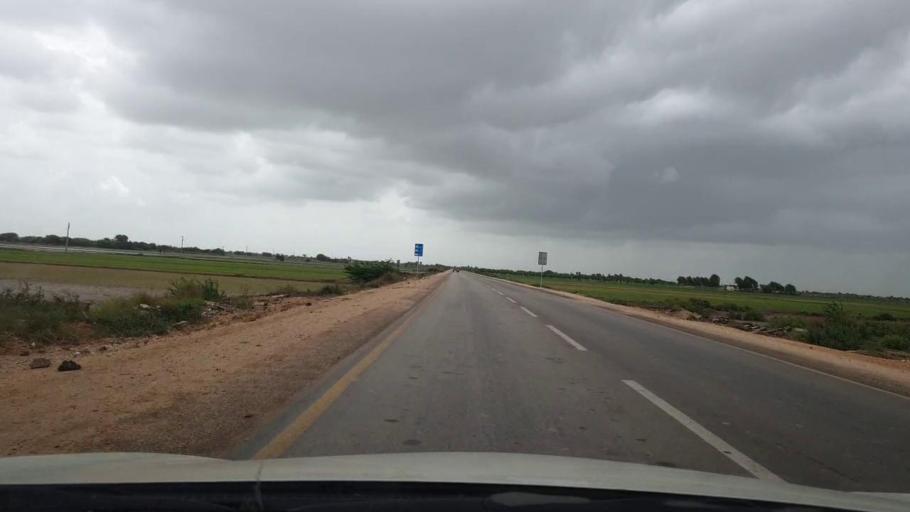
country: PK
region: Sindh
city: Mirpur Batoro
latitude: 24.6435
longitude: 68.4382
